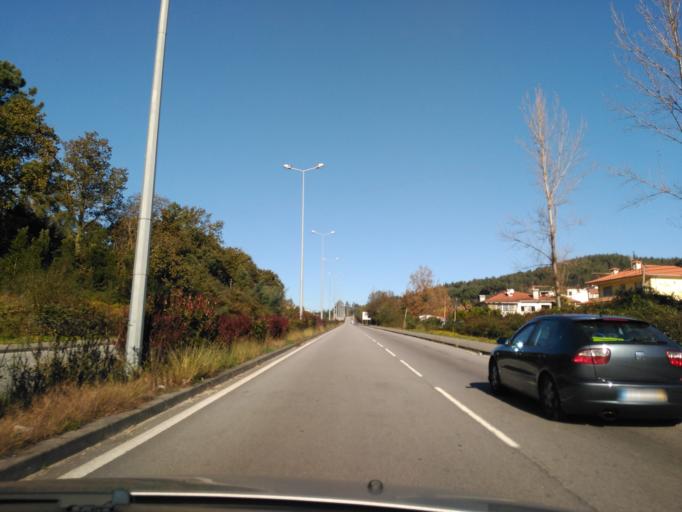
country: PT
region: Braga
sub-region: Braga
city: Adaufe
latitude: 41.5755
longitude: -8.3693
